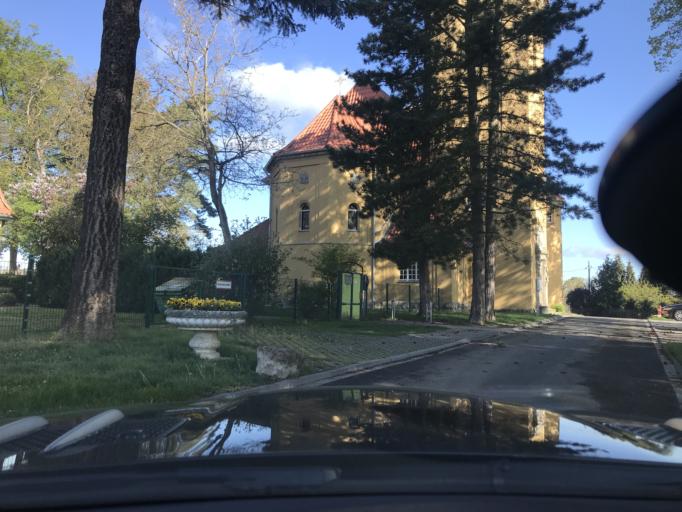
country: DE
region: Thuringia
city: Oberdorla
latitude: 51.2109
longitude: 10.3992
